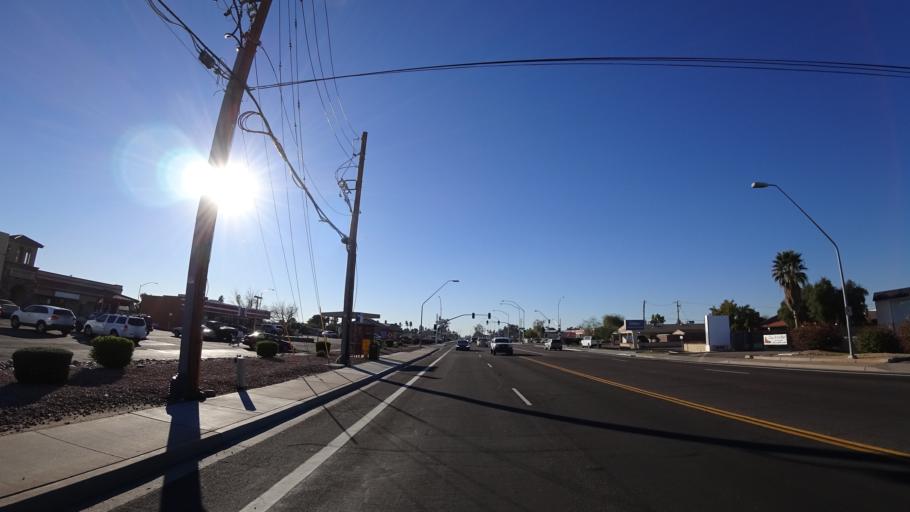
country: US
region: Arizona
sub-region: Maricopa County
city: Mesa
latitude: 33.3933
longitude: -111.8131
